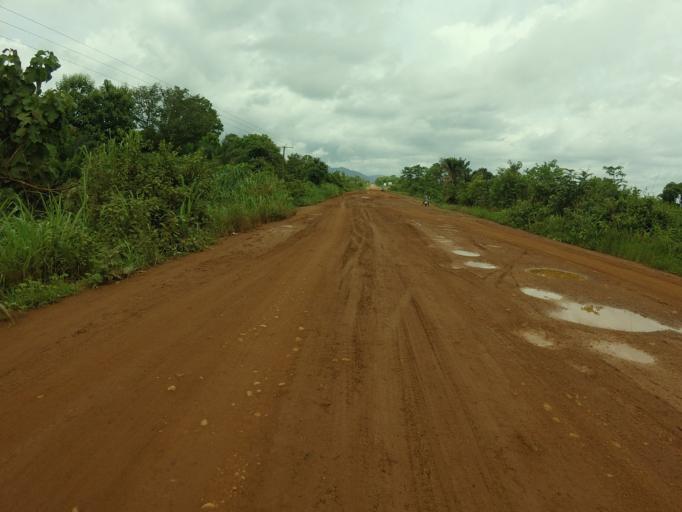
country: GH
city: Kpandae
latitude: 8.2792
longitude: 0.5070
